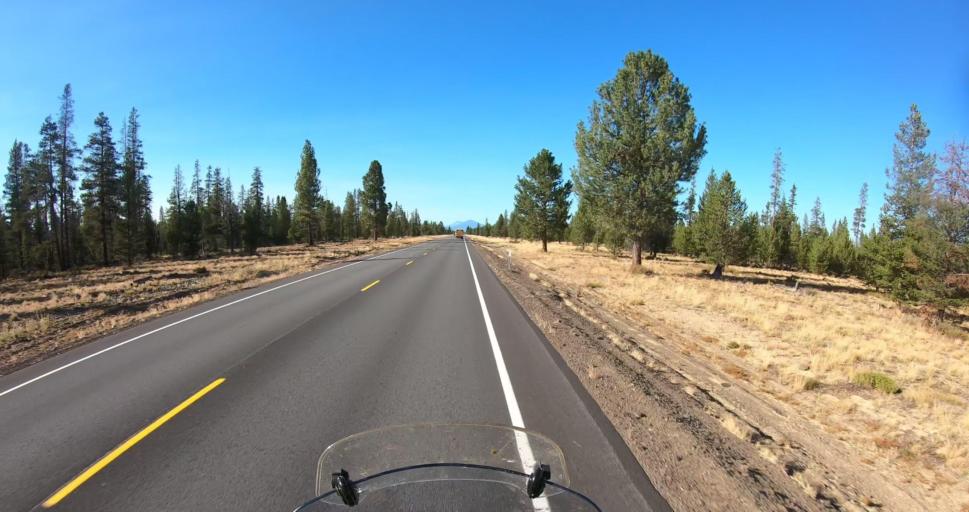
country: US
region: Oregon
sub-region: Deschutes County
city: La Pine
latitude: 43.5915
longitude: -121.4929
